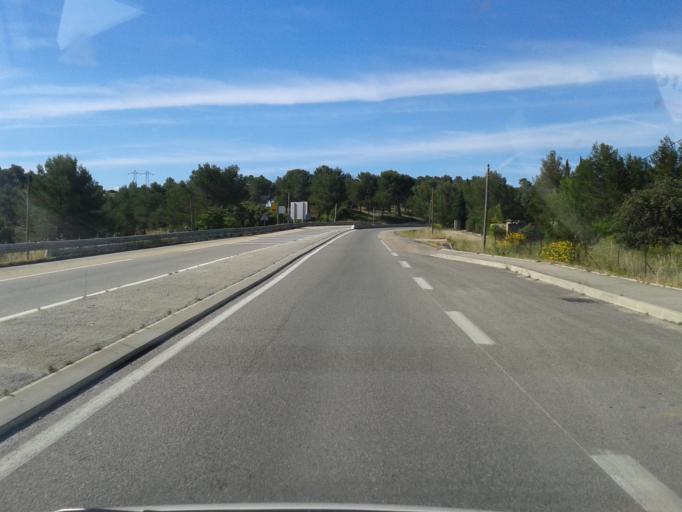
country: FR
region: Provence-Alpes-Cote d'Azur
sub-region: Departement des Bouches-du-Rhone
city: Meyrargues
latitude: 43.6347
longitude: 5.5168
